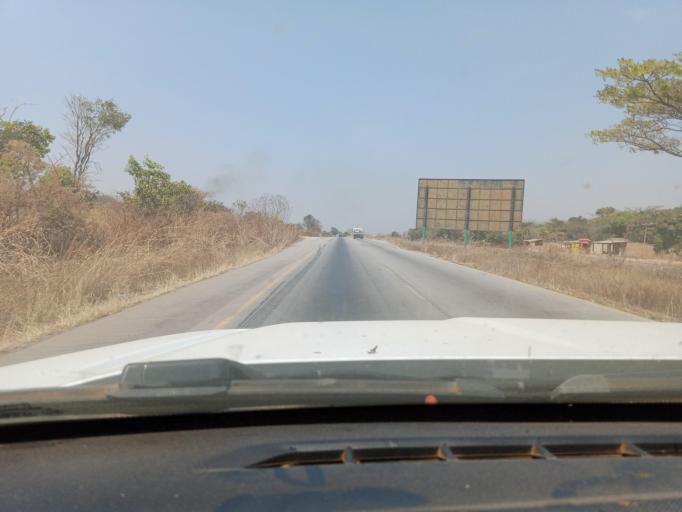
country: ZM
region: Copperbelt
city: Luanshya
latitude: -12.9962
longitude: 28.4201
